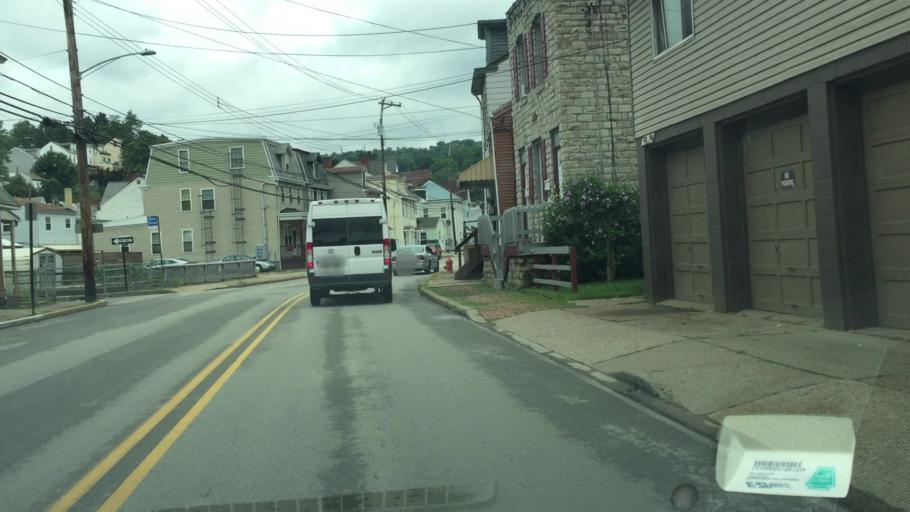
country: US
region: Pennsylvania
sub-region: Allegheny County
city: Millvale
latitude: 40.4877
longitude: -79.9726
